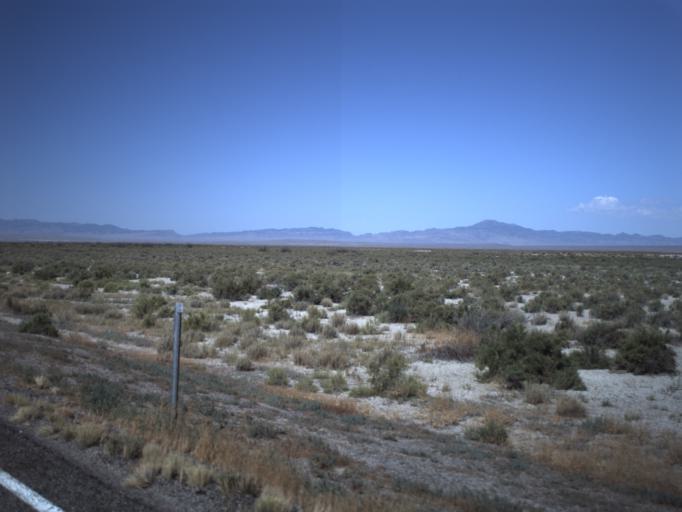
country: US
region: Utah
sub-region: Millard County
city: Delta
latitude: 39.3032
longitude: -112.8064
